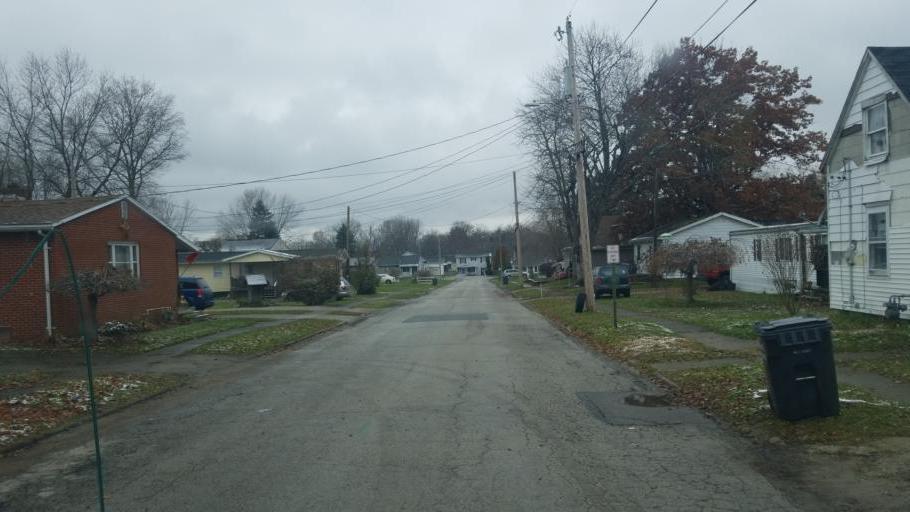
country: US
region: Ohio
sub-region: Richland County
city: Shelby
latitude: 40.8734
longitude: -82.6559
